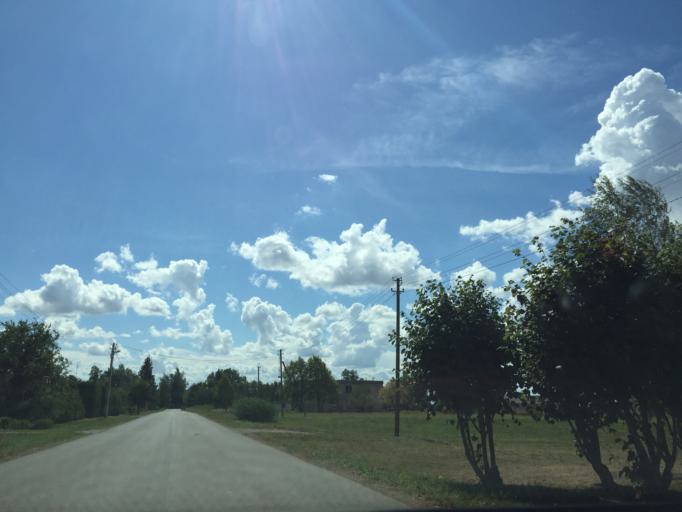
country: LV
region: Rundales
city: Pilsrundale
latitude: 56.3197
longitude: 23.9115
